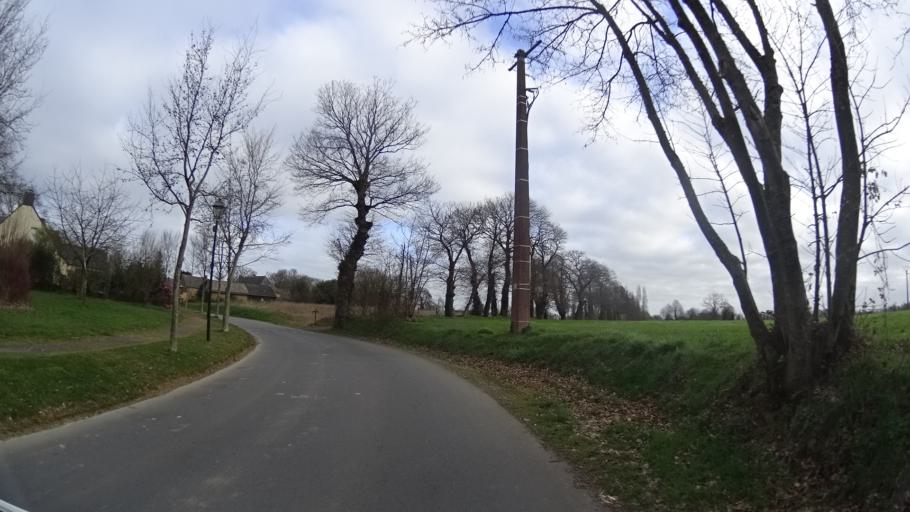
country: FR
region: Brittany
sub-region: Departement d'Ille-et-Vilaine
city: Saint-Gilles
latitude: 48.1793
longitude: -1.8526
